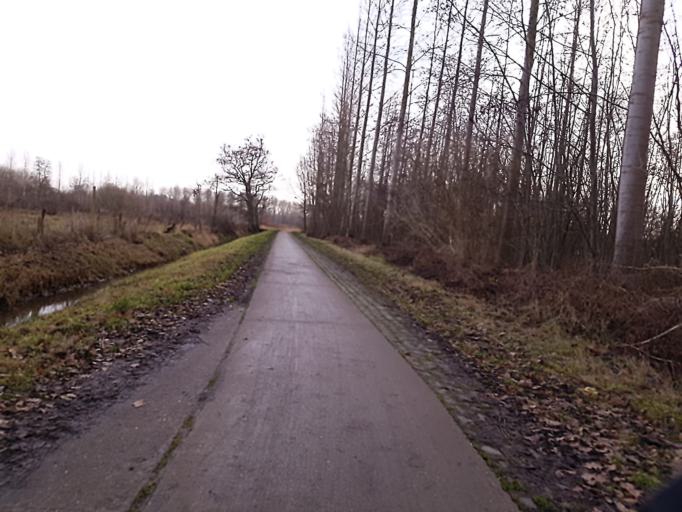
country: BE
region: Flanders
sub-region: Provincie Vlaams-Brabant
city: Rotselaar
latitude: 50.9420
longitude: 4.7022
